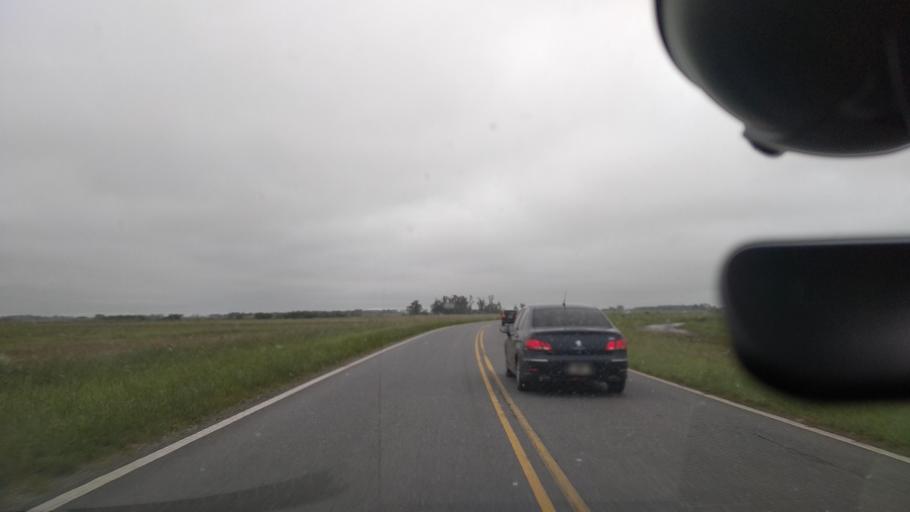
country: AR
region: Buenos Aires
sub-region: Partido de Magdalena
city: Magdalena
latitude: -35.2564
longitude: -57.6614
